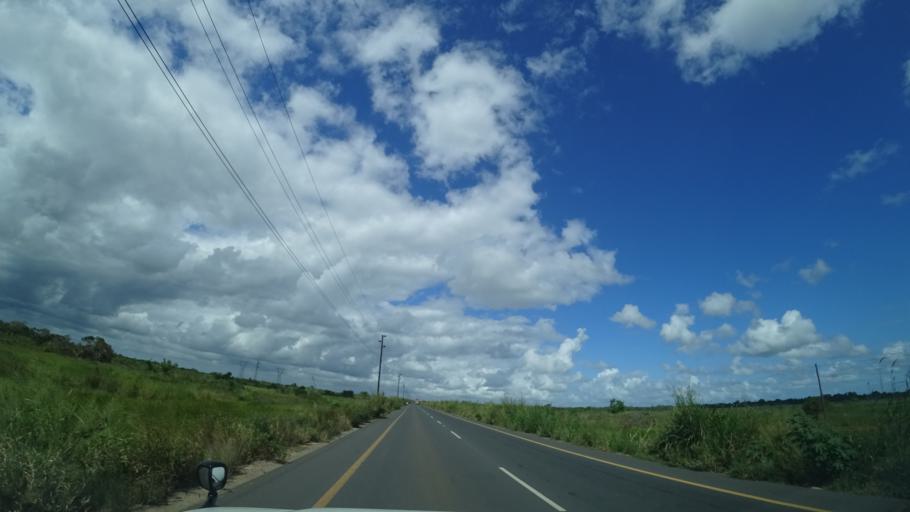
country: MZ
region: Sofala
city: Dondo
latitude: -19.5122
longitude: 34.6140
